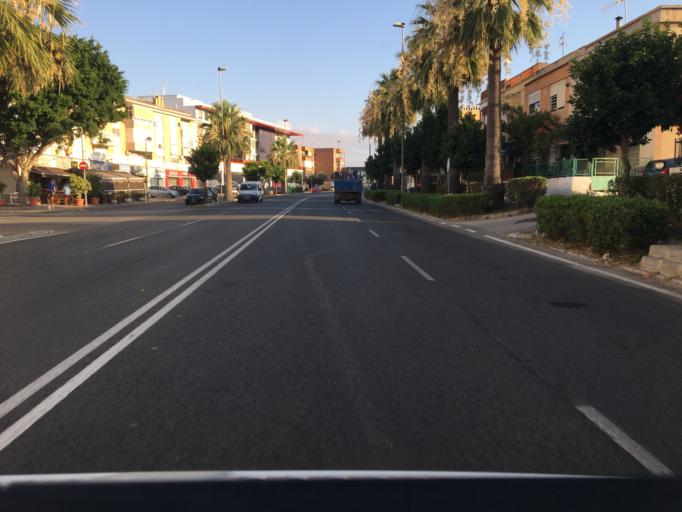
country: ES
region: Murcia
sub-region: Murcia
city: Cartagena
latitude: 37.6254
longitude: -1.0009
